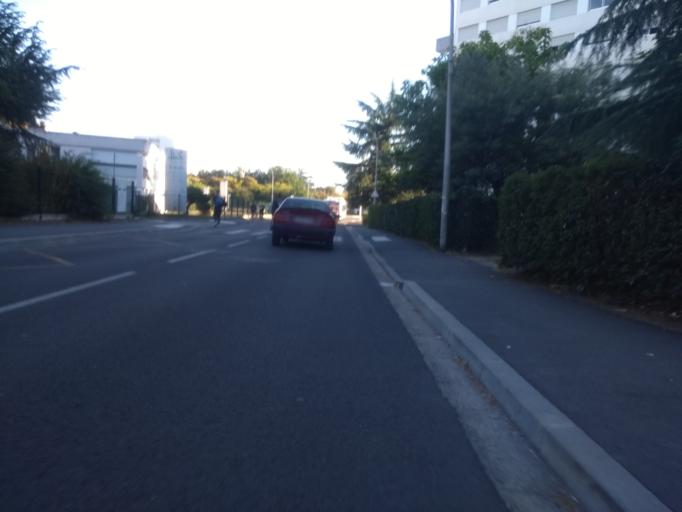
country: FR
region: Aquitaine
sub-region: Departement de la Gironde
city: Gradignan
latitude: 44.7914
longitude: -0.6130
